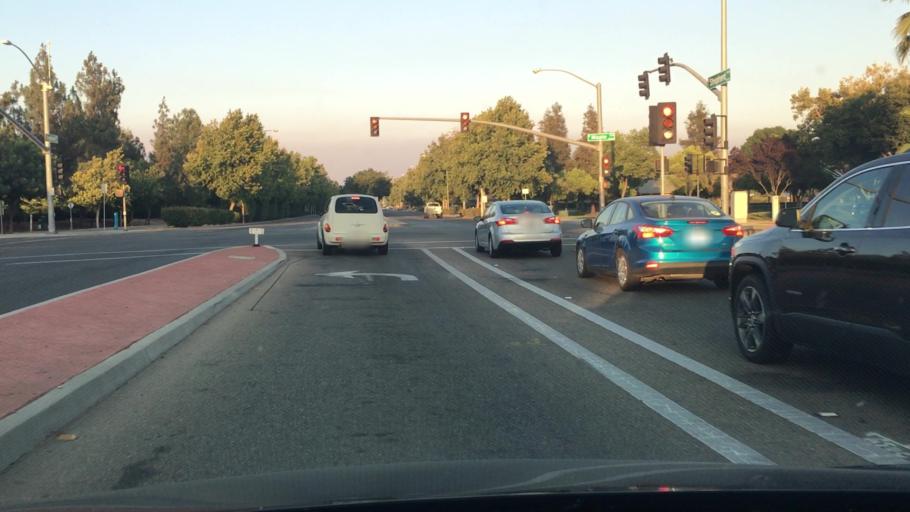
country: US
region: California
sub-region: Fresno County
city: Clovis
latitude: 36.8666
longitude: -119.7482
